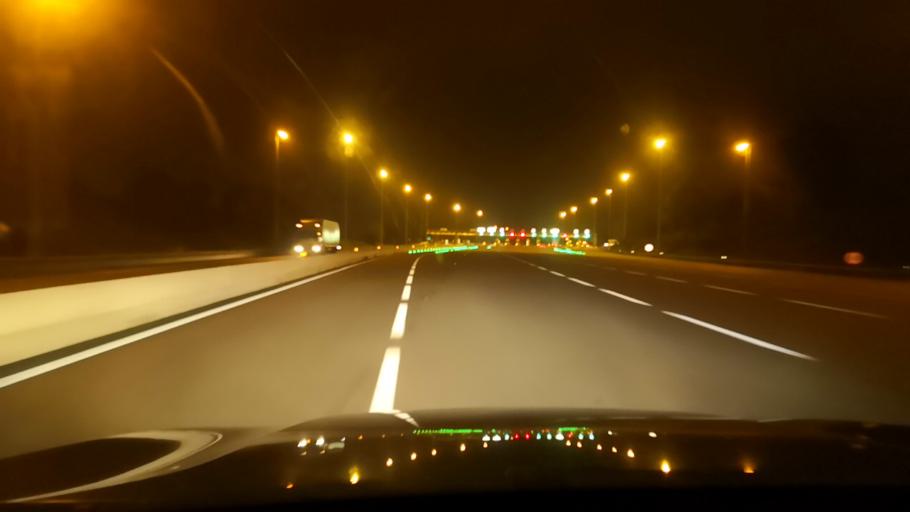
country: PT
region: Setubal
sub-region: Palmela
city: Palmela
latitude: 38.5719
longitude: -8.8666
